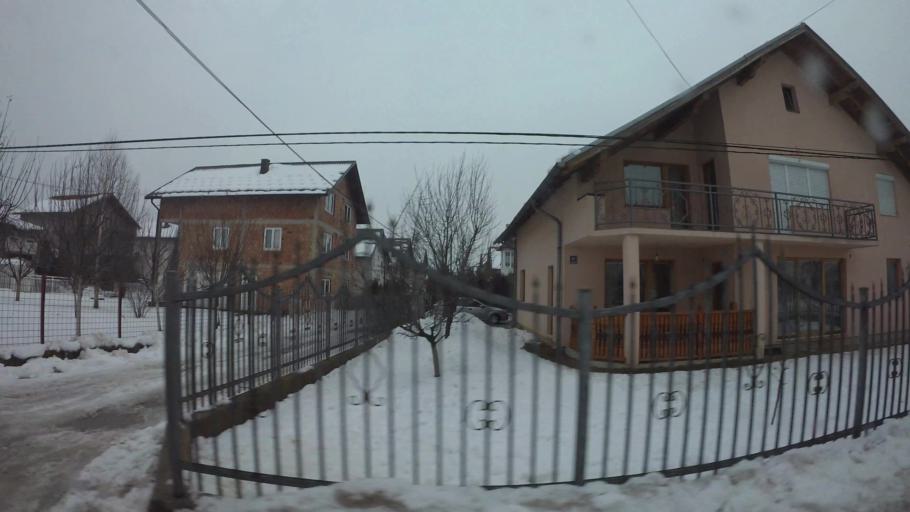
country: BA
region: Federation of Bosnia and Herzegovina
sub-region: Kanton Sarajevo
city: Sarajevo
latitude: 43.8446
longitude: 18.3063
